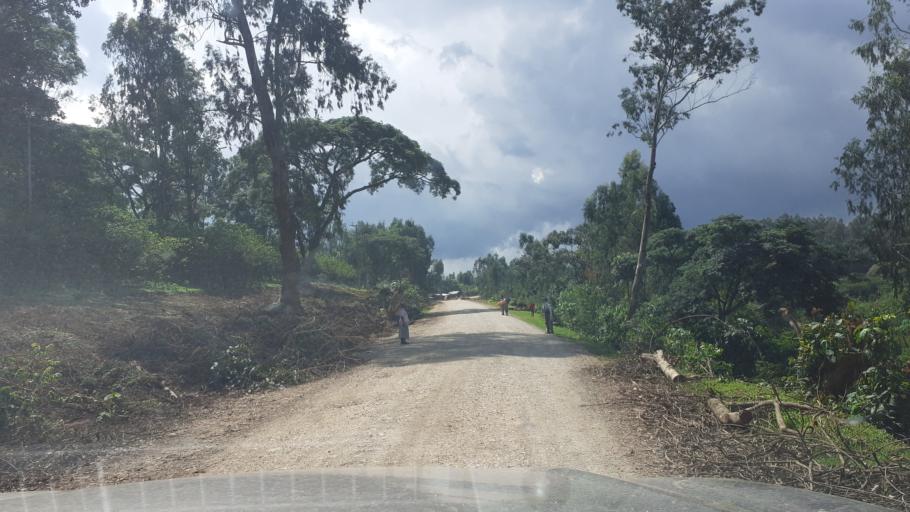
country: ET
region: Oromiya
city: Gimbi
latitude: 9.2856
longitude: 35.6884
